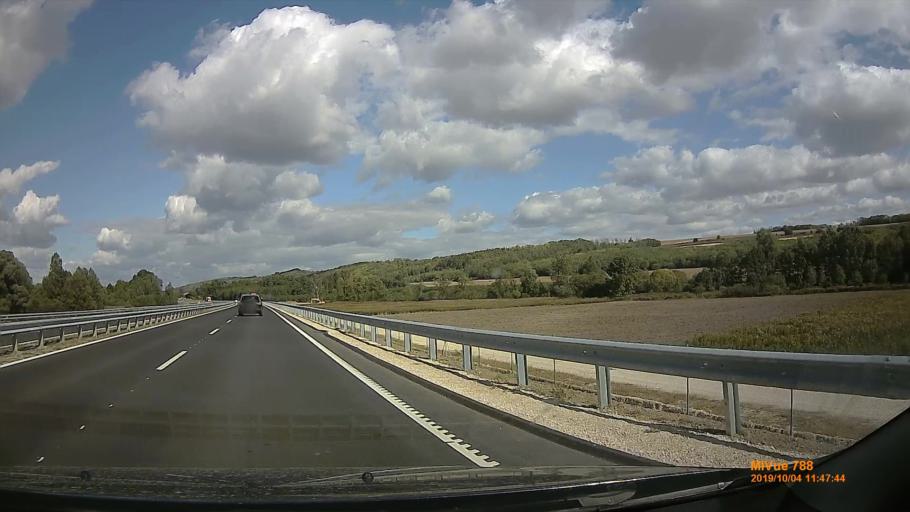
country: HU
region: Somogy
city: Karad
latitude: 46.6529
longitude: 17.7864
